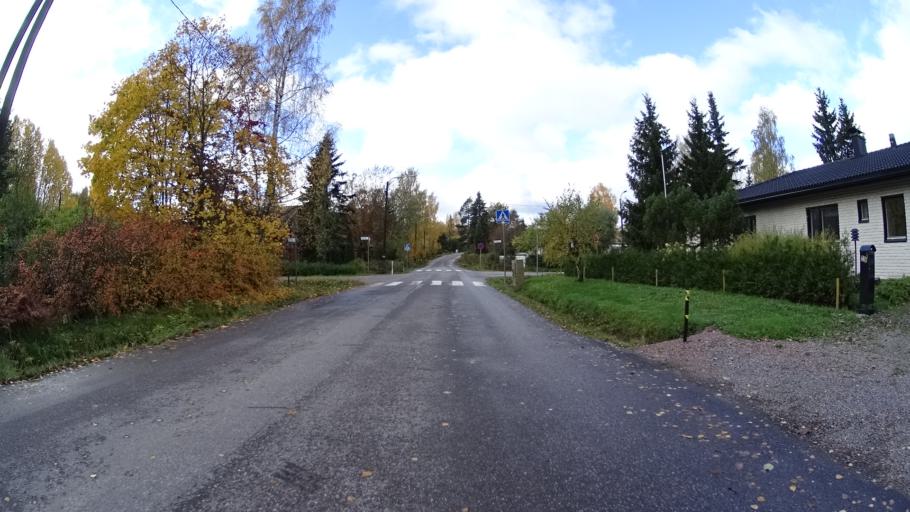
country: FI
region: Uusimaa
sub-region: Helsinki
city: Teekkarikylae
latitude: 60.2757
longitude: 24.8613
